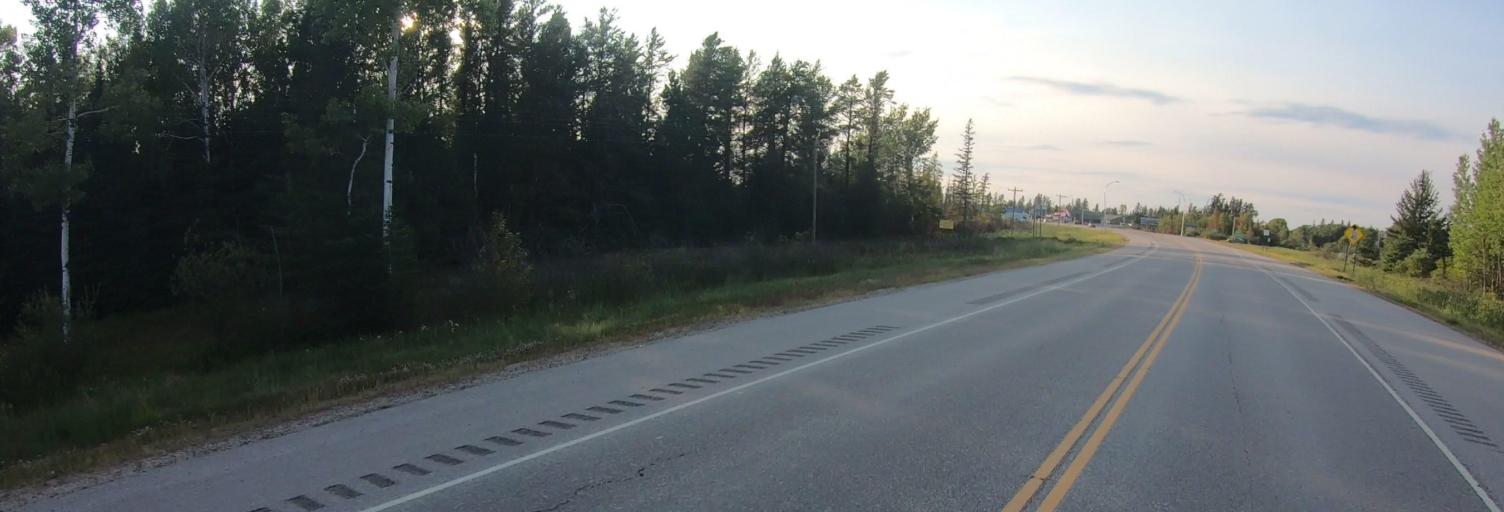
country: US
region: Minnesota
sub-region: Saint Louis County
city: Mountain Iron
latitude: 47.8402
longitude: -92.6807
